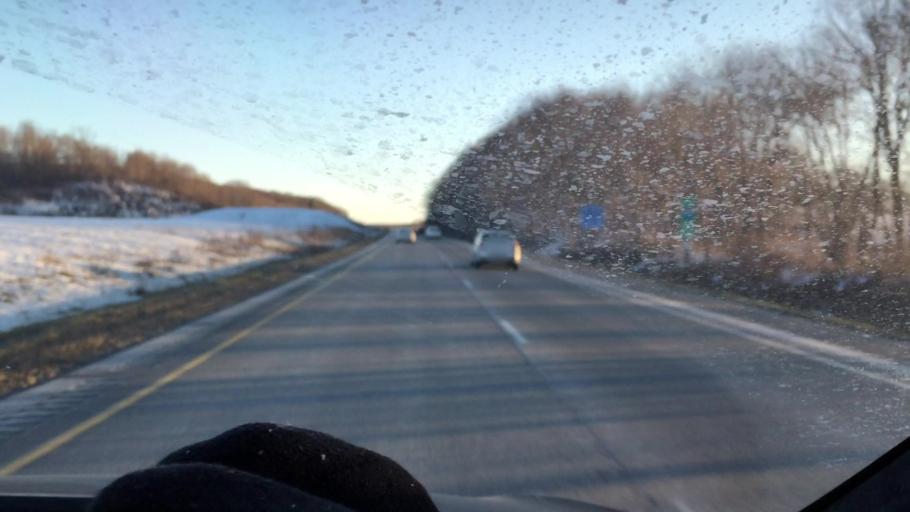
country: US
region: Pennsylvania
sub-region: Crawford County
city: Meadville
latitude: 41.6887
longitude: -80.2052
